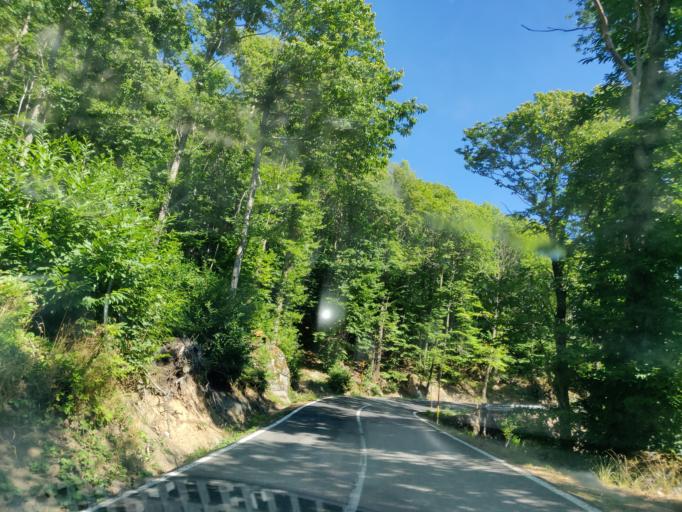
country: IT
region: Tuscany
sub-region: Provincia di Siena
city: Abbadia San Salvatore
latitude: 42.8991
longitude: 11.6493
